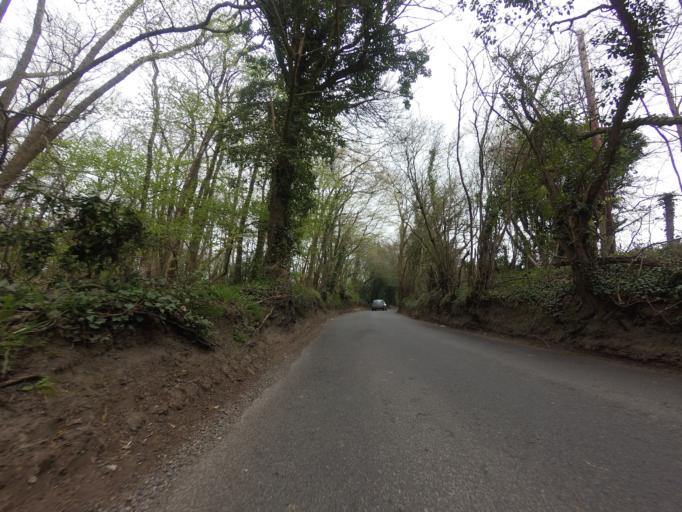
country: GB
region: England
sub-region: Greater London
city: Orpington
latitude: 51.3838
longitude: 0.1296
